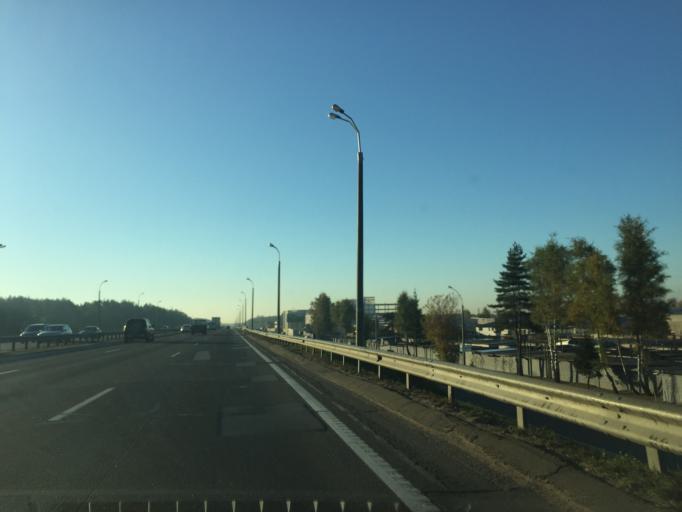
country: BY
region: Minsk
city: Vyaliki Trastsyanets
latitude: 53.9111
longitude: 27.6852
